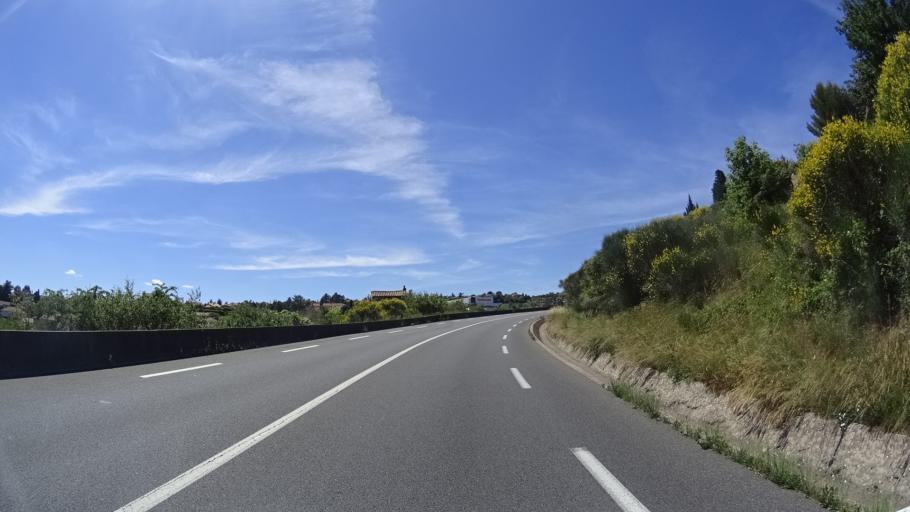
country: FR
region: Midi-Pyrenees
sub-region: Departement de l'Aveyron
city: Millau
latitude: 44.1136
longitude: 3.0766
